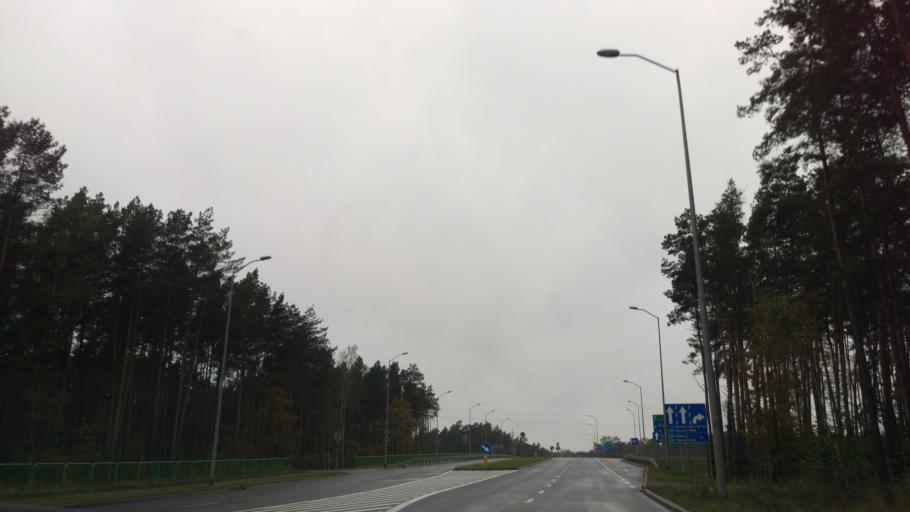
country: PL
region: West Pomeranian Voivodeship
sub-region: Powiat gryfinski
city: Stare Czarnowo
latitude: 53.3944
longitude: 14.7220
